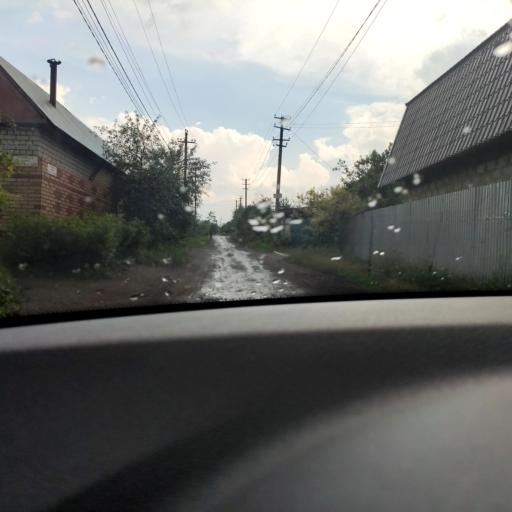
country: RU
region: Samara
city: Novosemeykino
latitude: 53.4004
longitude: 50.3143
